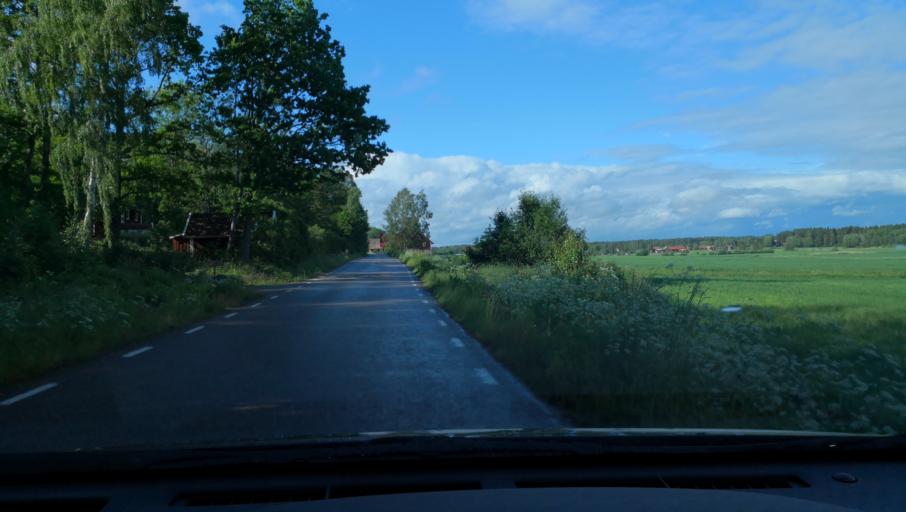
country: SE
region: OErebro
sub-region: Lindesbergs Kommun
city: Fellingsbro
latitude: 59.3116
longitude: 15.6777
